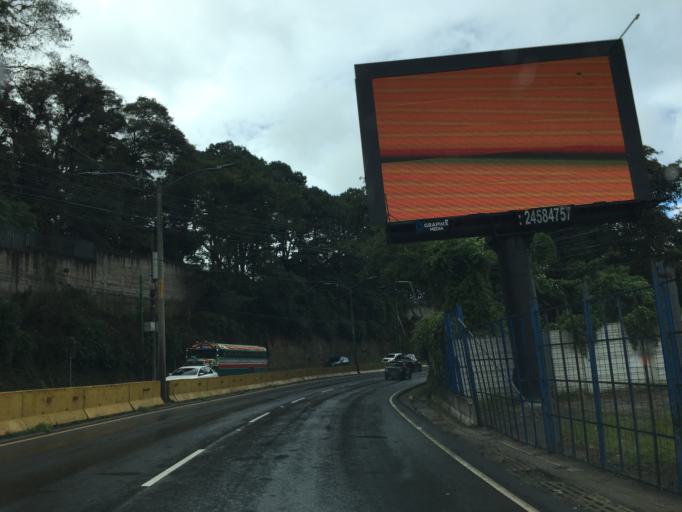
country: GT
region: Guatemala
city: Santa Catarina Pinula
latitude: 14.5778
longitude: -90.4854
